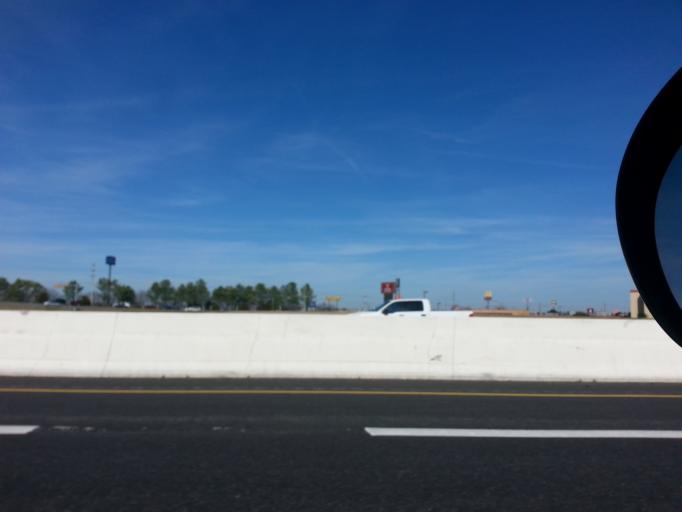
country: US
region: Tennessee
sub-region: Rutherford County
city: Murfreesboro
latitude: 35.8463
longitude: -86.4344
